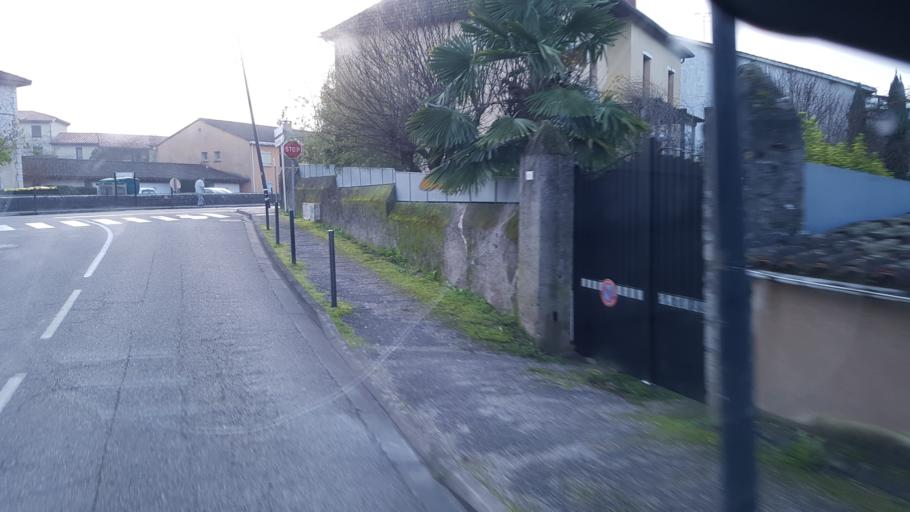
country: FR
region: Midi-Pyrenees
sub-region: Departement du Tarn-et-Garonne
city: Caussade
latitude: 44.1643
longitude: 1.5359
